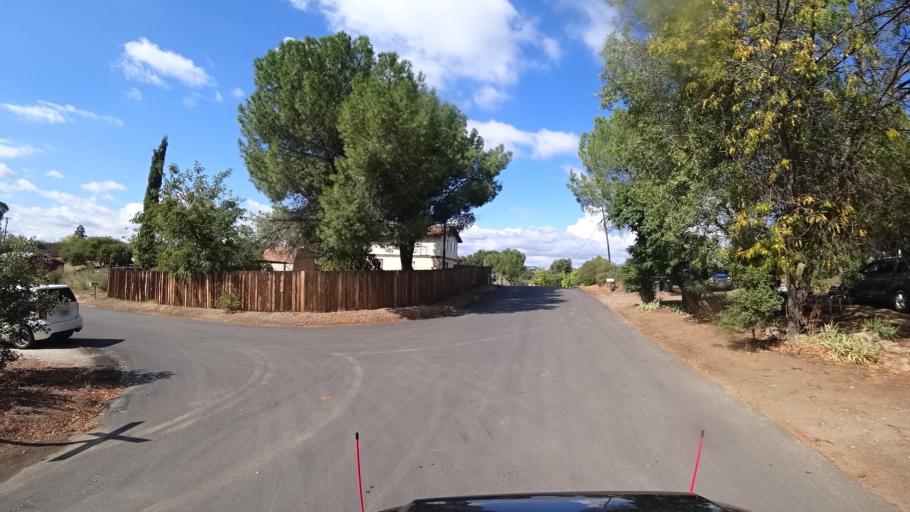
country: US
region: California
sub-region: San Diego County
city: Campo
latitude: 32.6794
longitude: -116.5014
